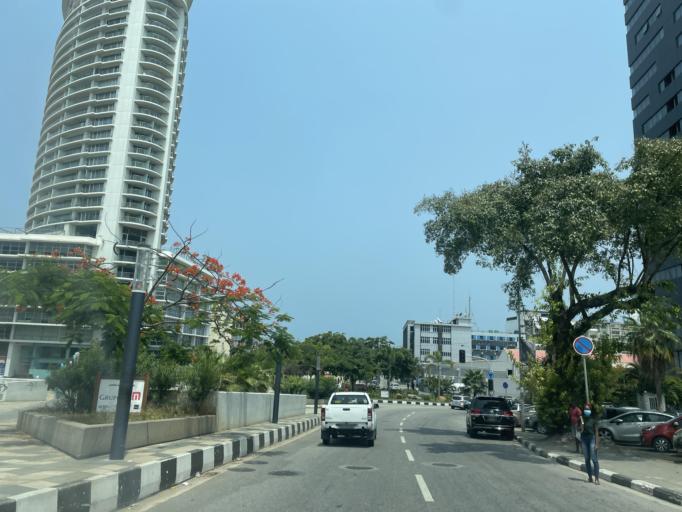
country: AO
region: Luanda
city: Luanda
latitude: -8.8090
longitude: 13.2403
